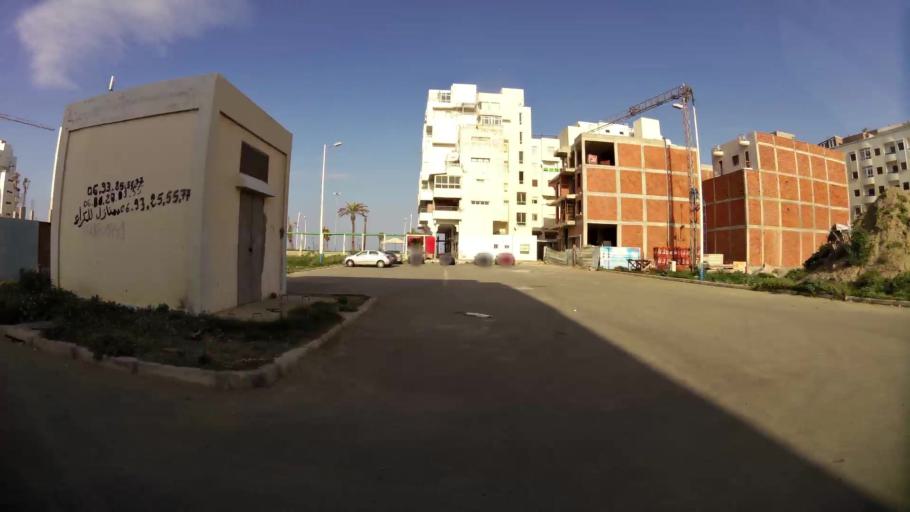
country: MA
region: Tanger-Tetouan
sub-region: Tetouan
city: Martil
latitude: 35.6301
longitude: -5.2758
